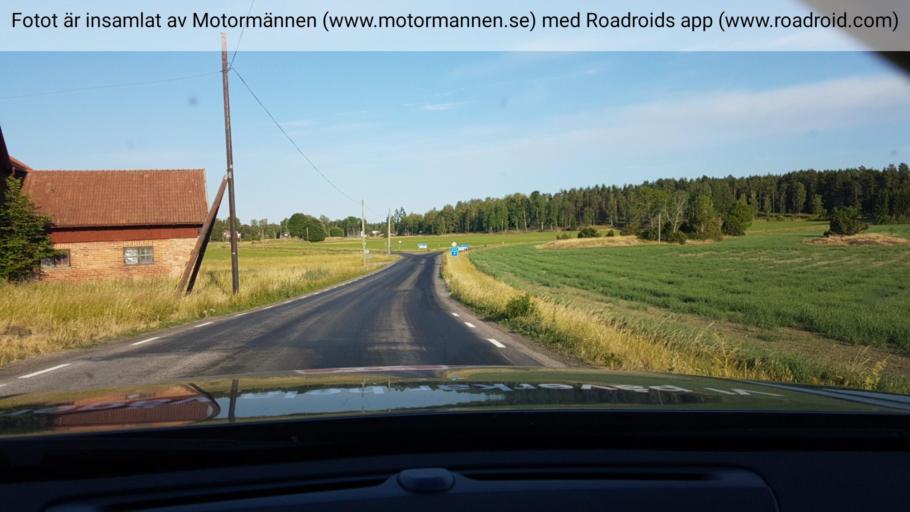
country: SE
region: Uppsala
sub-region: Osthammars Kommun
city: Gimo
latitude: 60.0277
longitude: 18.0555
